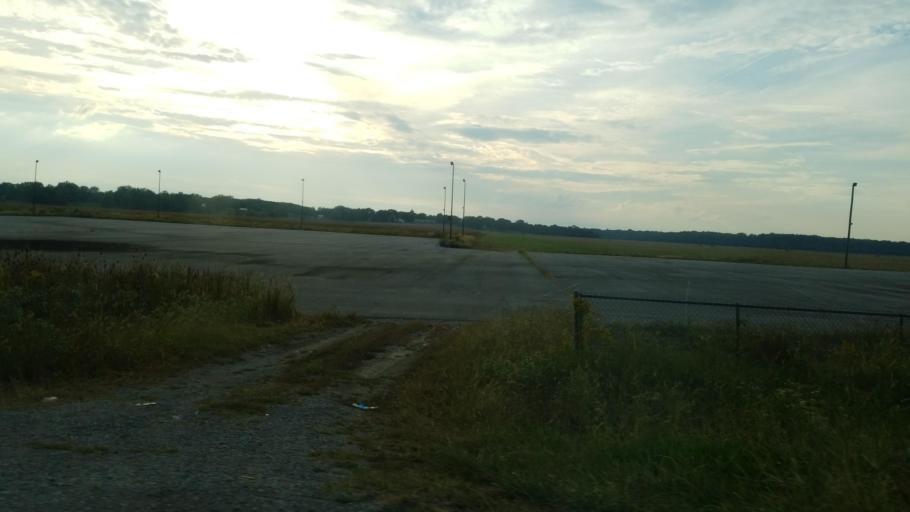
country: US
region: Illinois
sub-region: Saline County
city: Harrisburg
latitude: 37.7569
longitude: -88.5402
